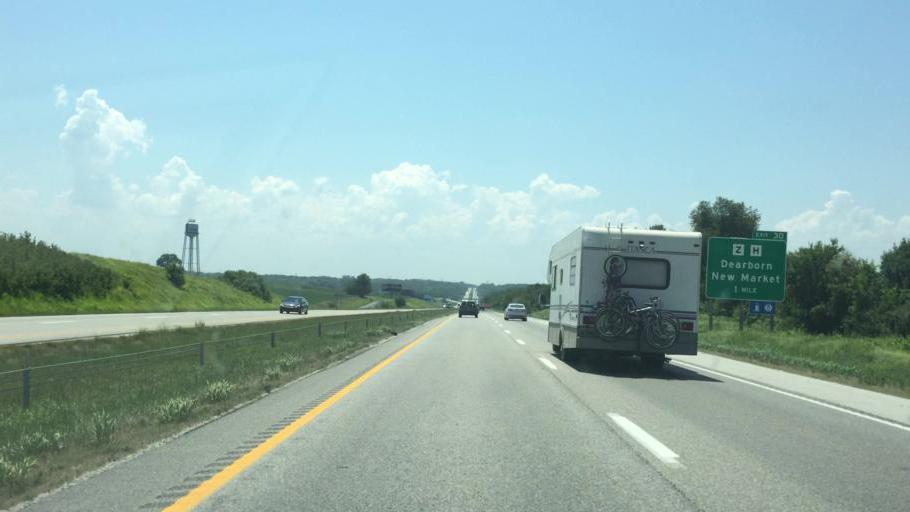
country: US
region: Missouri
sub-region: Platte County
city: Platte City
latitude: 39.5334
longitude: -94.7874
